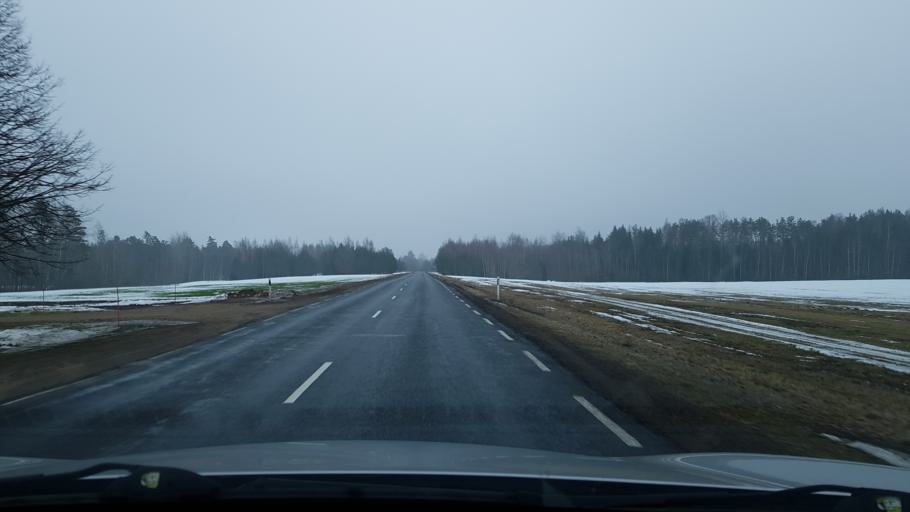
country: EE
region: Valgamaa
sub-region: Torva linn
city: Torva
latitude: 58.1269
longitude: 25.9924
